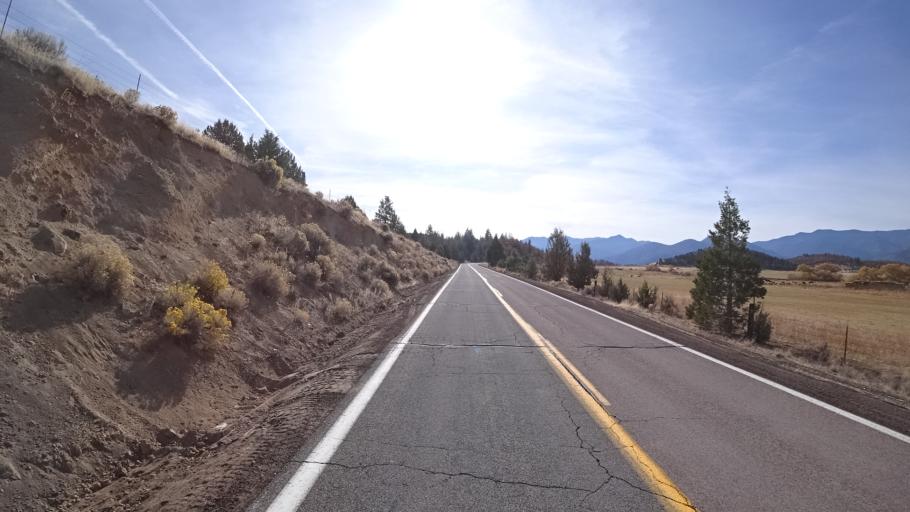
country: US
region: California
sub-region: Siskiyou County
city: Weed
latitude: 41.4790
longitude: -122.4109
